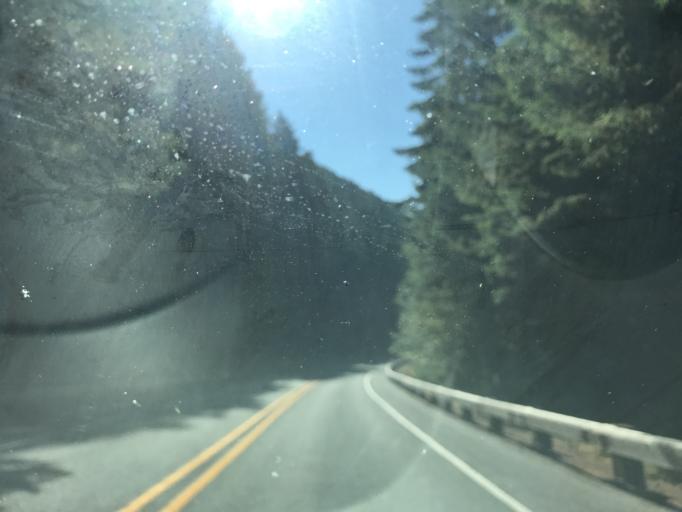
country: US
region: Washington
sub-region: King County
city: Enumclaw
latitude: 47.0227
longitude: -121.5344
